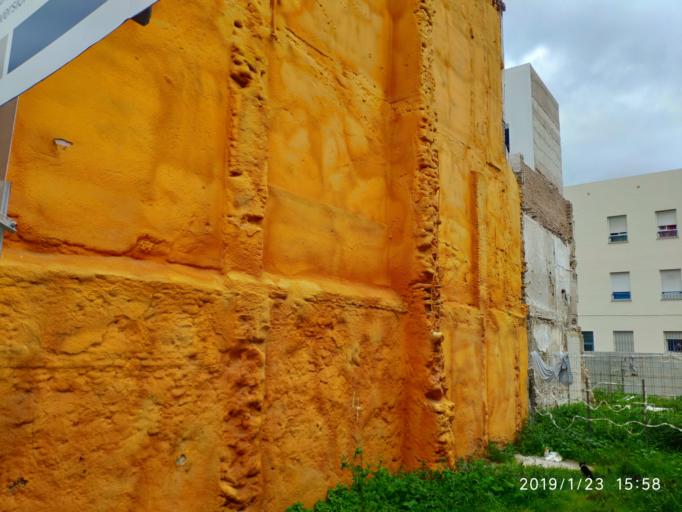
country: ES
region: Andalusia
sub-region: Provincia de Malaga
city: Malaga
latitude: 36.7259
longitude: -4.4240
